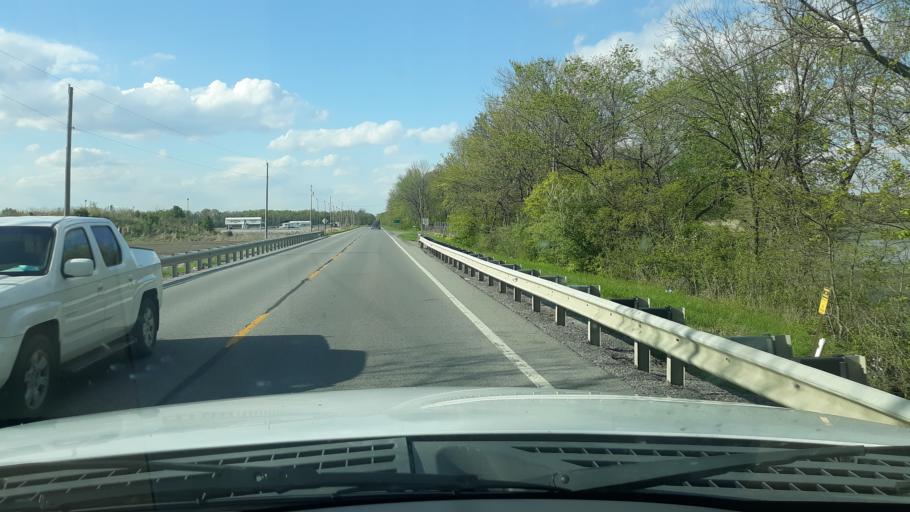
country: US
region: Illinois
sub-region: Saline County
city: Harrisburg
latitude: 37.7540
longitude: -88.5403
